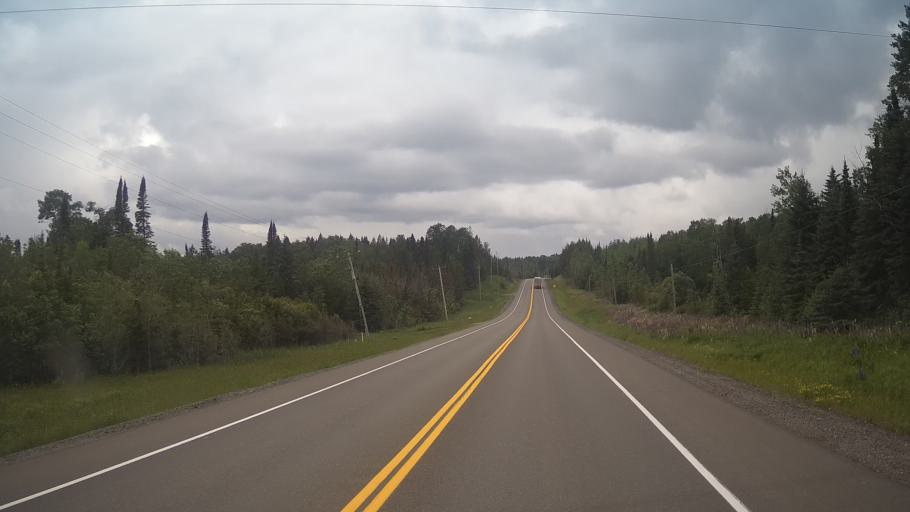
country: CA
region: Ontario
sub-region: Thunder Bay District
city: Thunder Bay
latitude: 48.5093
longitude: -89.4684
